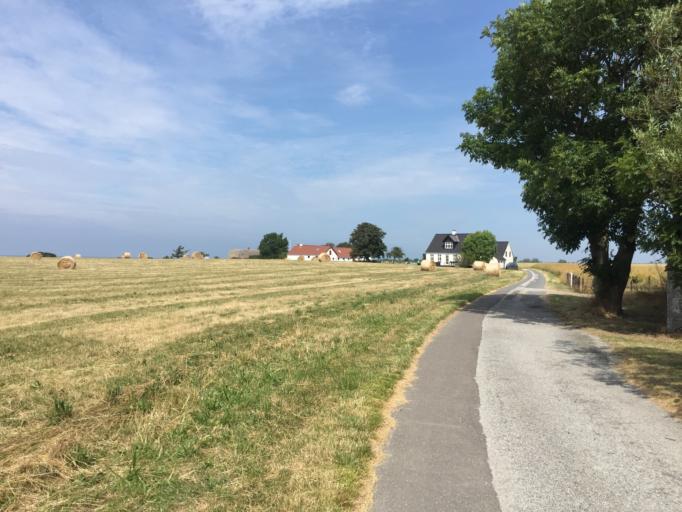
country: DK
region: Zealand
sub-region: Slagelse Kommune
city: Skaelskor
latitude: 55.1972
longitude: 11.1826
